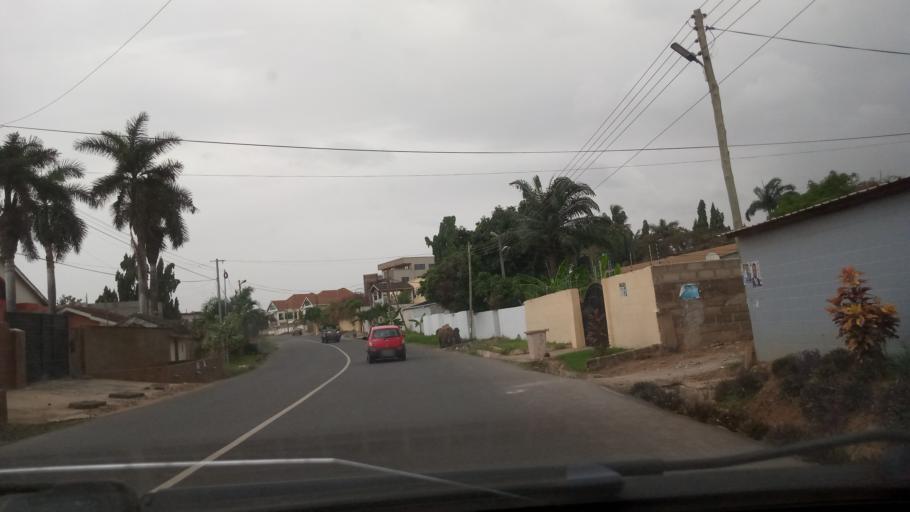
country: GH
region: Greater Accra
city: Dome
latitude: 5.6156
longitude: -0.2017
